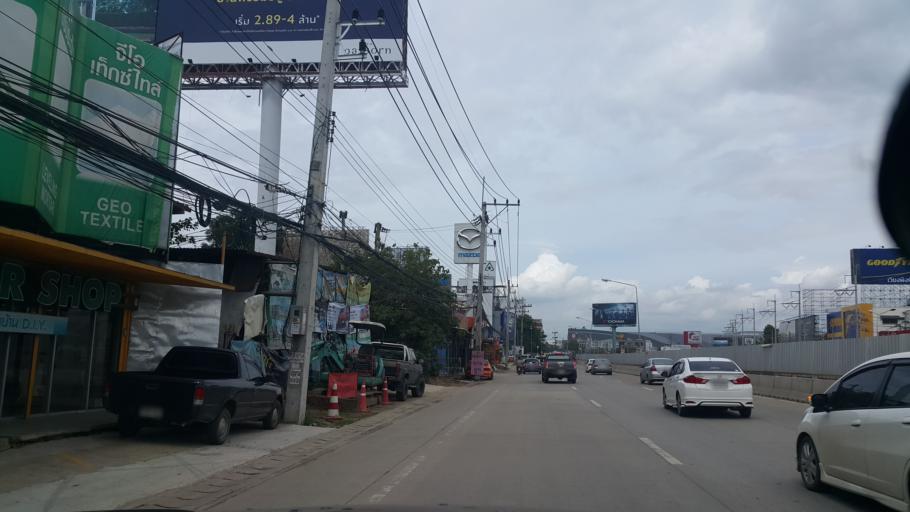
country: TH
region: Chiang Mai
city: Chiang Mai
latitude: 18.8100
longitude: 99.0088
